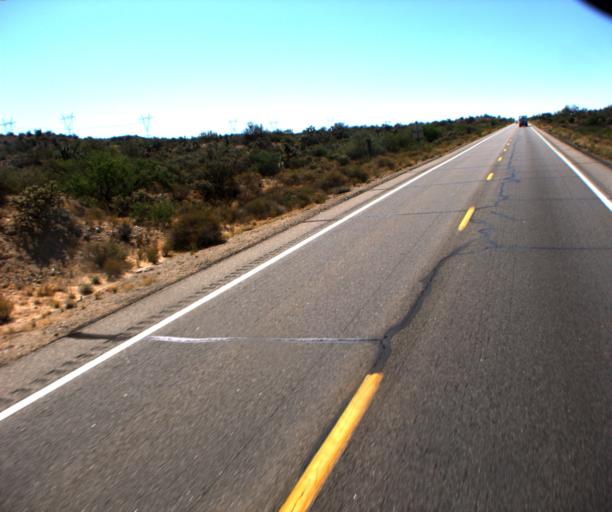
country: US
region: Arizona
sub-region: Yavapai County
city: Bagdad
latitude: 34.3558
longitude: -113.1685
